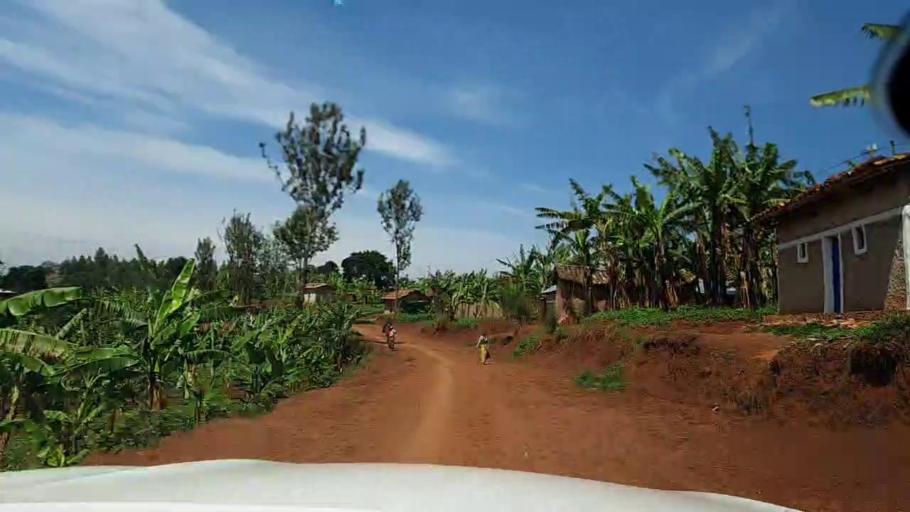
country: RW
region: Southern Province
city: Butare
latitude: -2.7058
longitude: 29.8415
